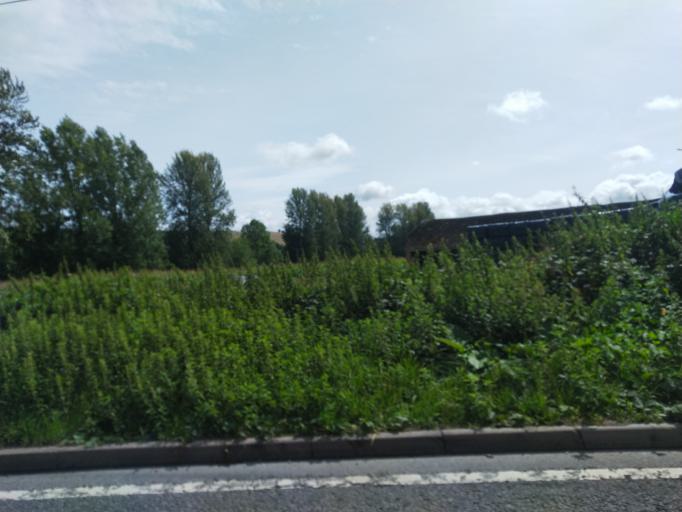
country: GB
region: England
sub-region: Dorset
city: Blandford Forum
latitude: 50.8976
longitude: -2.1963
